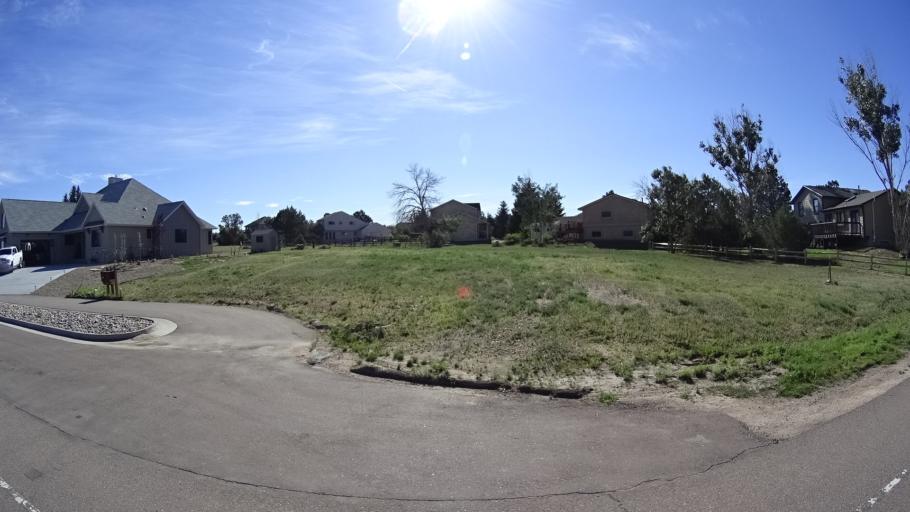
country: US
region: Colorado
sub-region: El Paso County
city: Gleneagle
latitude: 39.0344
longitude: -104.8282
